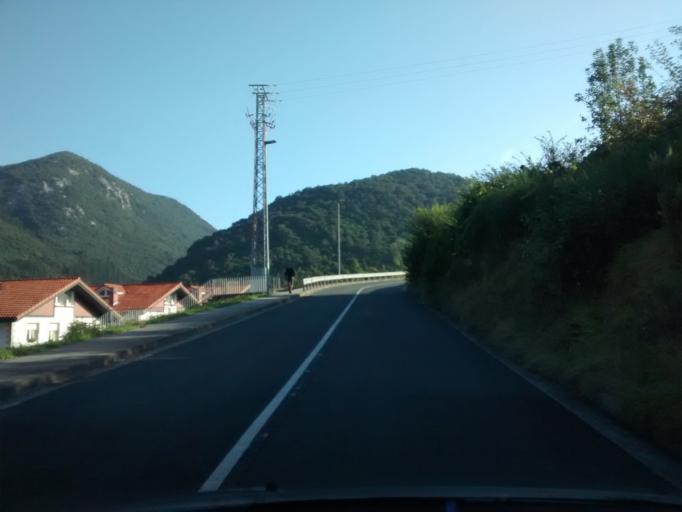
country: ES
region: Basque Country
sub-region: Provincia de Guipuzcoa
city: Mendaro
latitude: 43.2501
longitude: -2.3875
